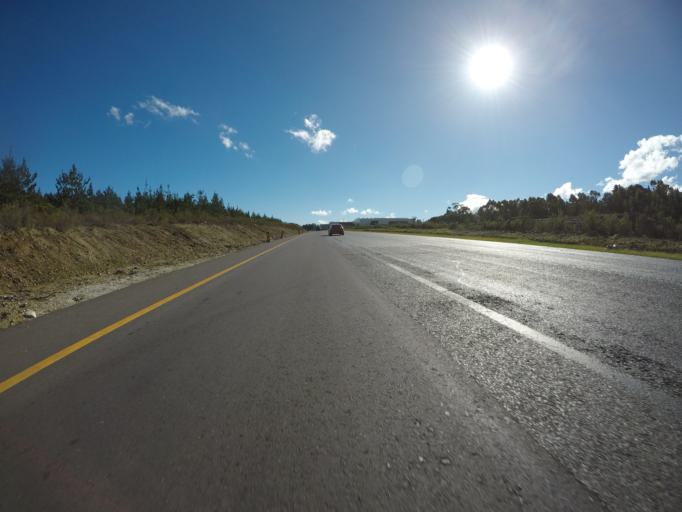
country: ZA
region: Western Cape
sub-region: Overberg District Municipality
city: Grabouw
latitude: -34.1810
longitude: 19.0811
